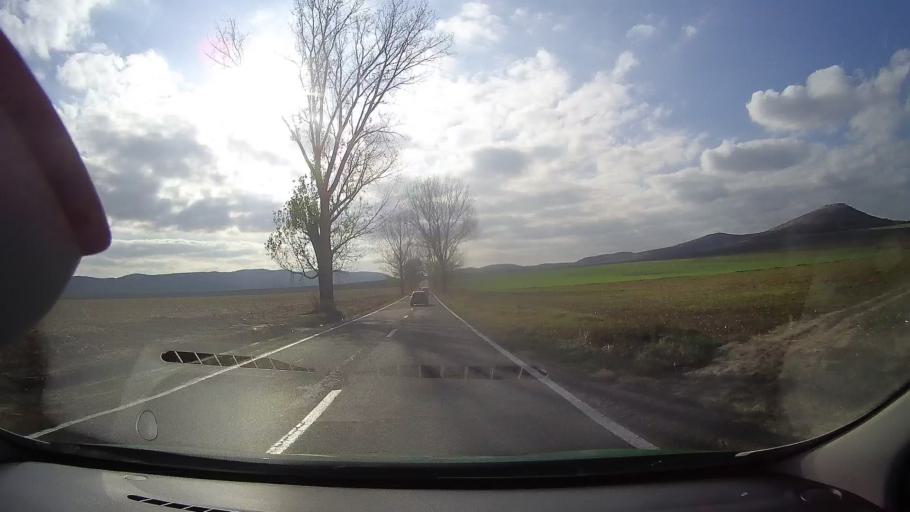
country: RO
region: Tulcea
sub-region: Comuna Nalbant
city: Nicolae Balcescu
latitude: 44.9898
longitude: 28.5608
